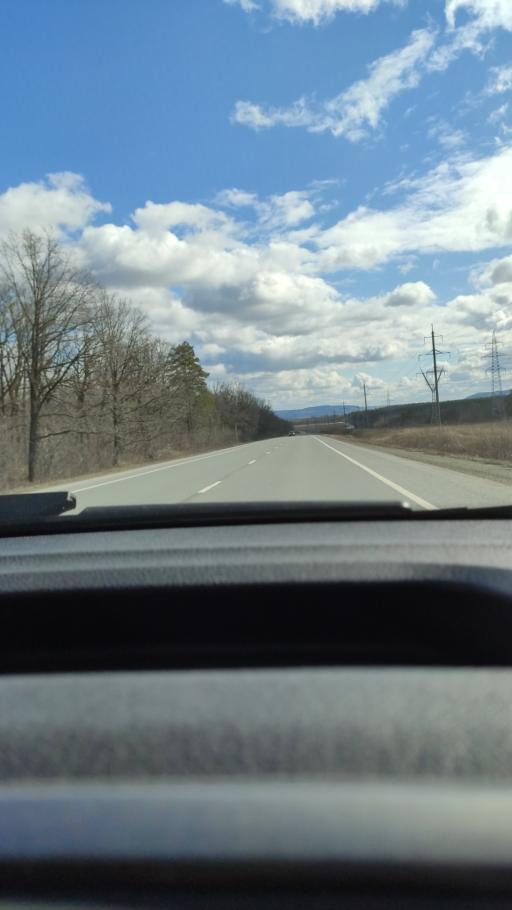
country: RU
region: Samara
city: Bogatyr'
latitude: 53.5008
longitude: 49.9514
